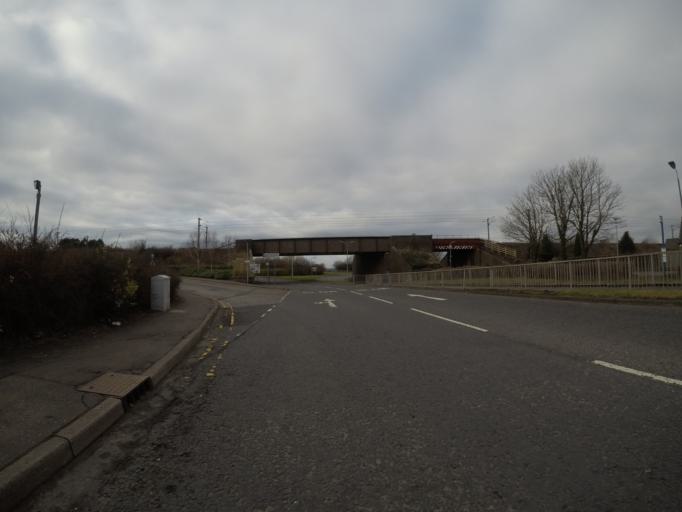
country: GB
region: Scotland
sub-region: North Ayrshire
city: Irvine
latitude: 55.6137
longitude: -4.6750
